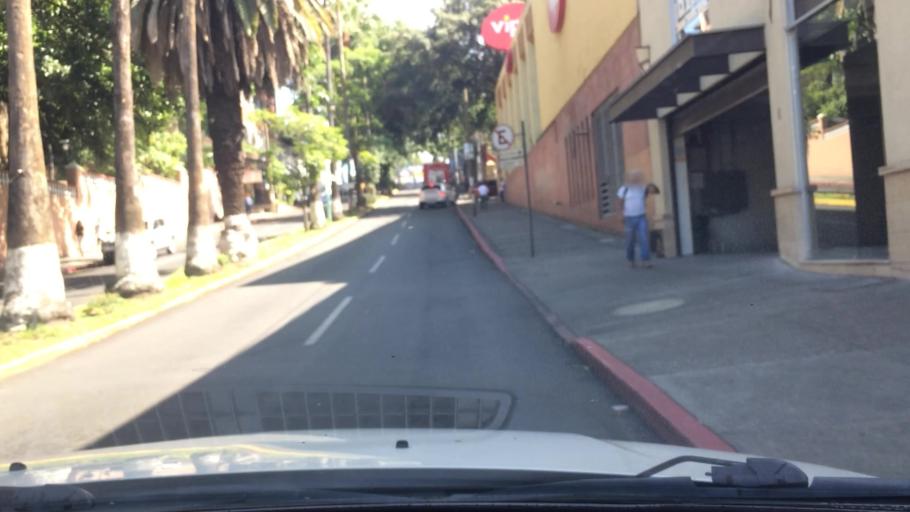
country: MX
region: Morelos
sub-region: Cuernavaca
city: Cuernavaca
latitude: 18.9190
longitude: -99.2337
